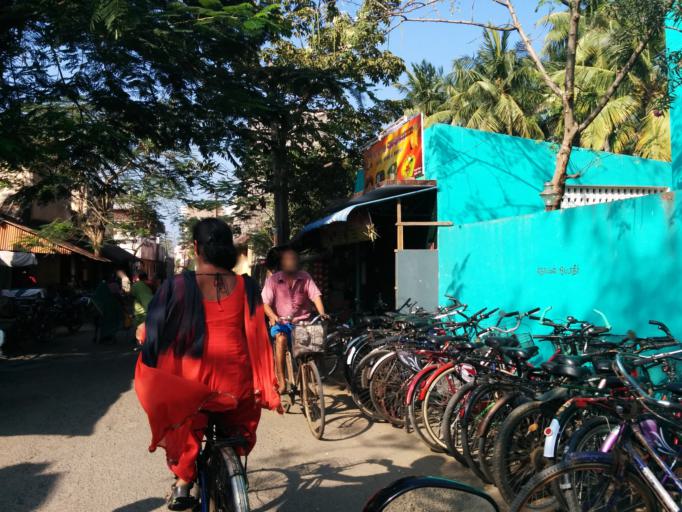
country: IN
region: Pondicherry
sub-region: Puducherry
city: Puducherry
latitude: 11.9479
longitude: 79.8348
